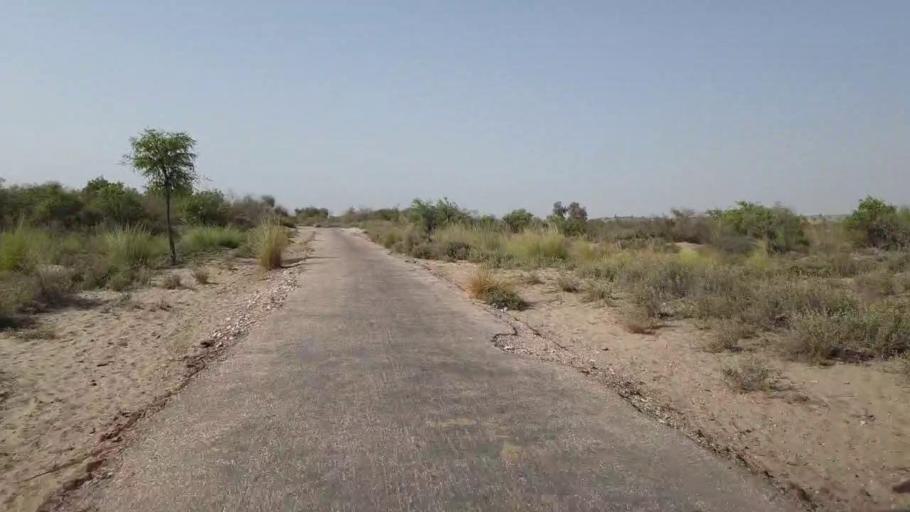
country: PK
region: Sindh
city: Jam Sahib
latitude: 26.5902
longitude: 68.9220
